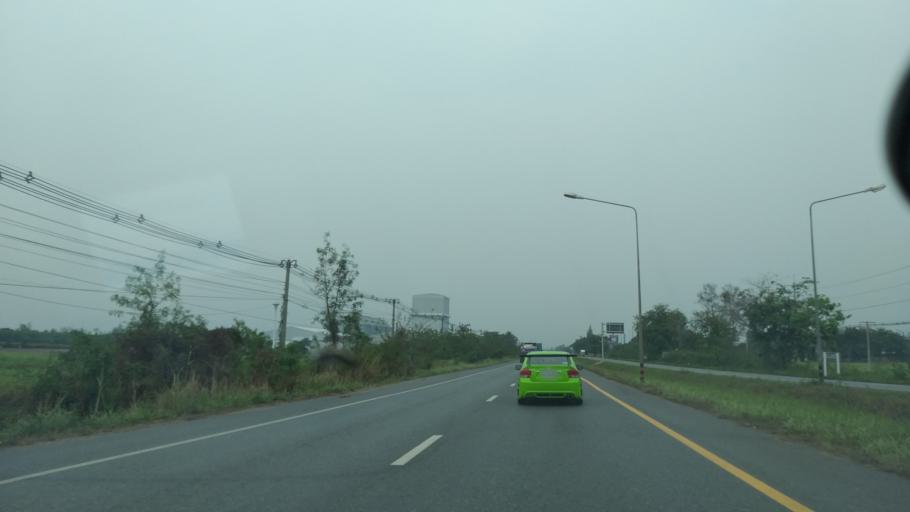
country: TH
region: Chon Buri
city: Ko Chan
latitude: 13.3567
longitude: 101.2722
